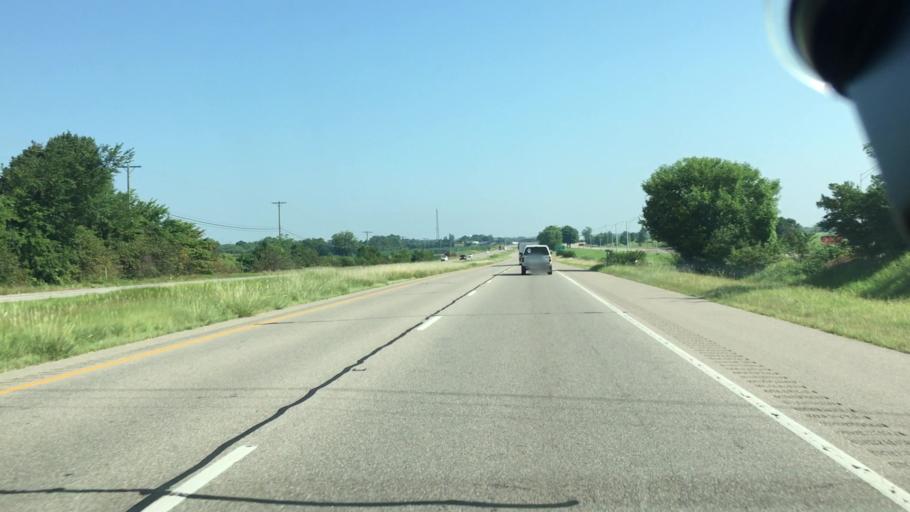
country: US
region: Indiana
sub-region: Gibson County
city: Fort Branch
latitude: 38.2922
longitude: -87.5674
